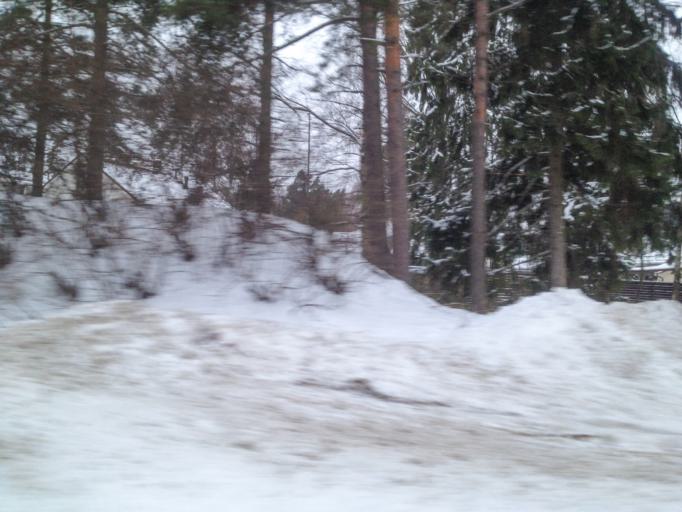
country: FI
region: Uusimaa
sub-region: Helsinki
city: Vantaa
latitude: 60.2092
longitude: 25.1359
